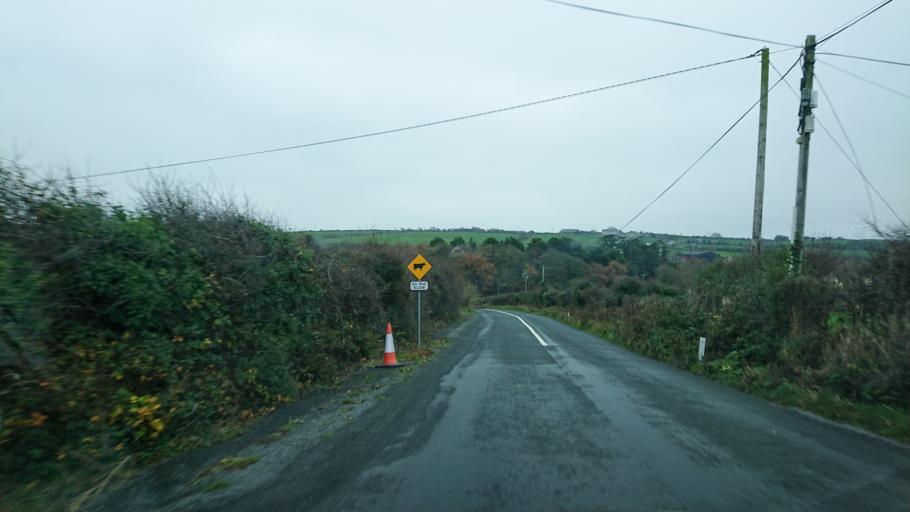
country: IE
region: Munster
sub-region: Waterford
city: Dunmore East
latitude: 52.1627
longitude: -7.0628
